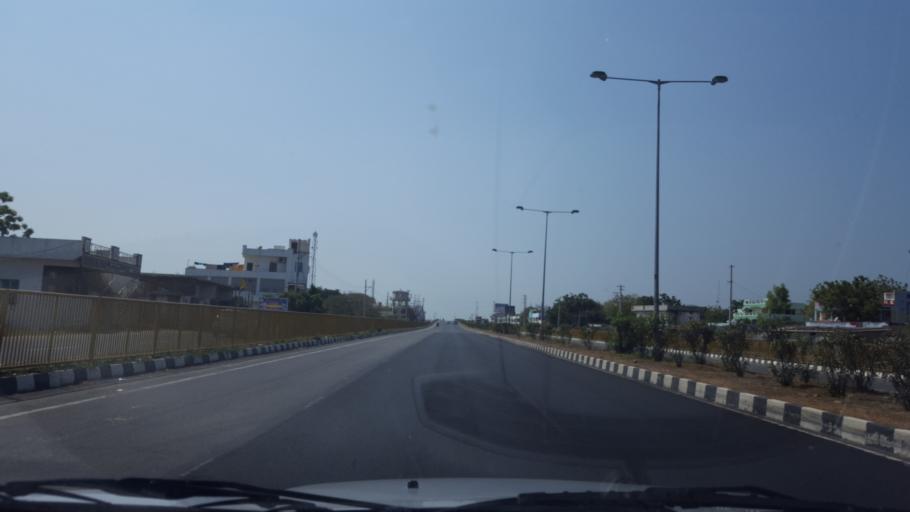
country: IN
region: Andhra Pradesh
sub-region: Guntur
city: Chilakalurupet
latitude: 15.9906
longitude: 80.1064
